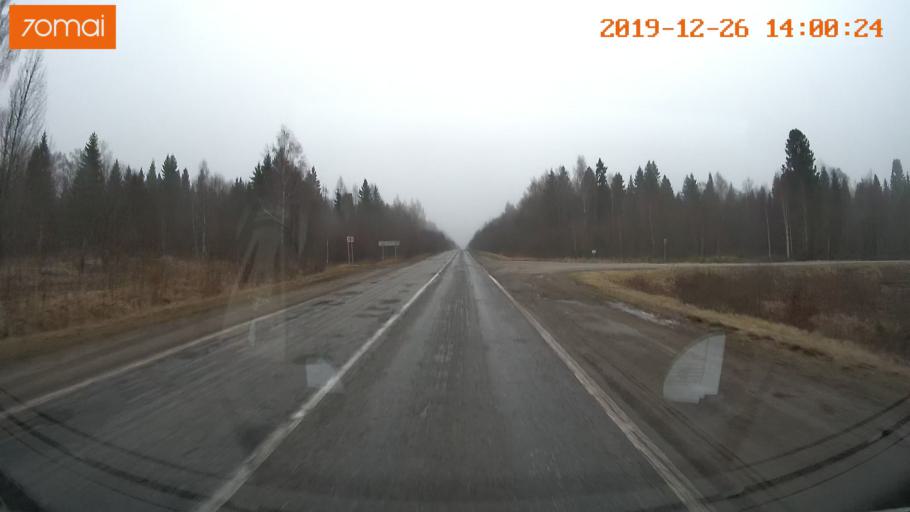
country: RU
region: Jaroslavl
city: Poshekhon'ye
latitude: 58.5584
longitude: 38.7426
